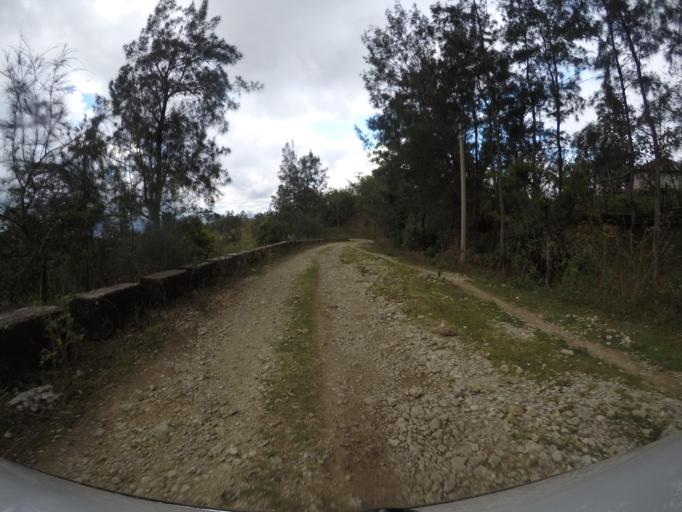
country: TL
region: Baucau
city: Venilale
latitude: -8.6718
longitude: 126.6301
